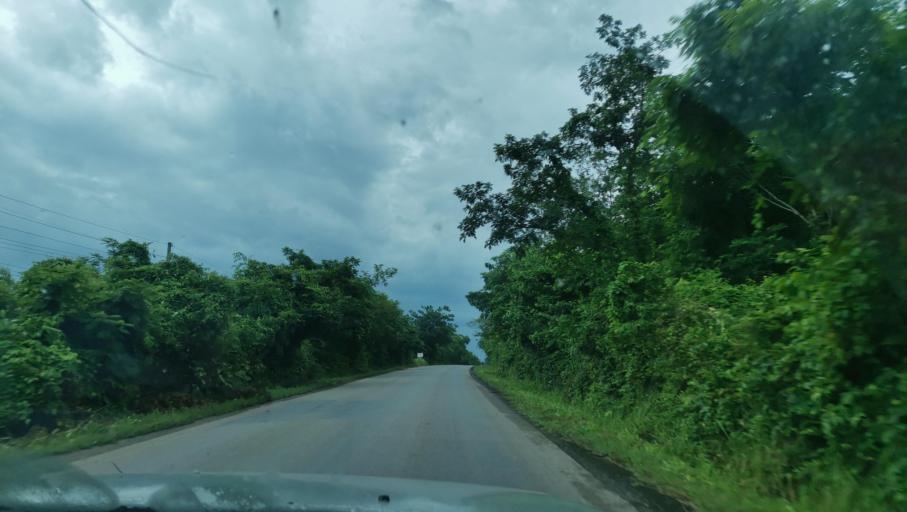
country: TH
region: Nakhon Phanom
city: Ban Phaeng
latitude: 17.8688
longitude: 104.4180
